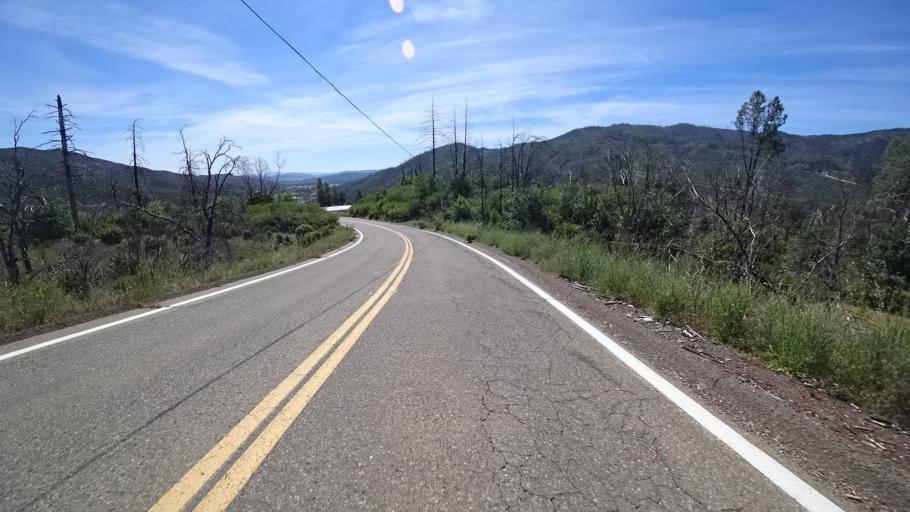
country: US
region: California
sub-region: Lake County
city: Cobb
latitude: 38.7808
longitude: -122.6910
